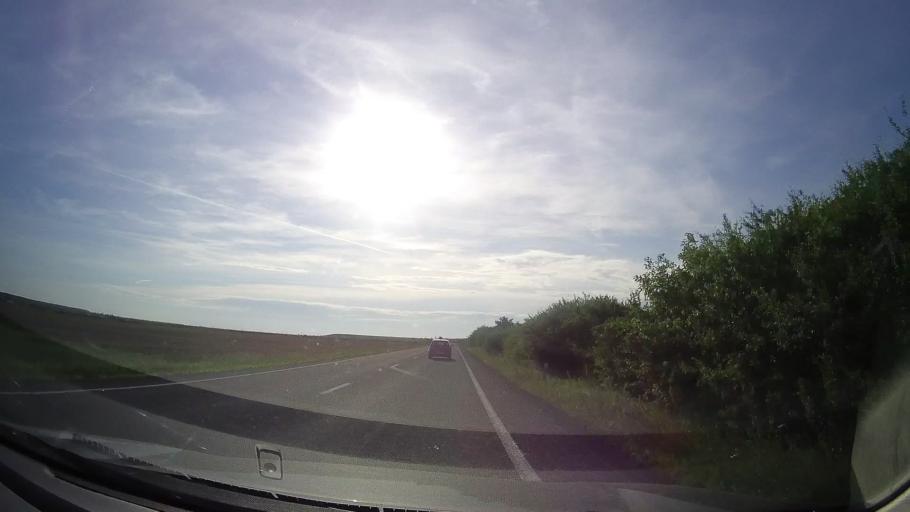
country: RO
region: Timis
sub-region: Comuna Topolovatu Mare
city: Topolovatu Mare
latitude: 45.7927
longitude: 21.5612
